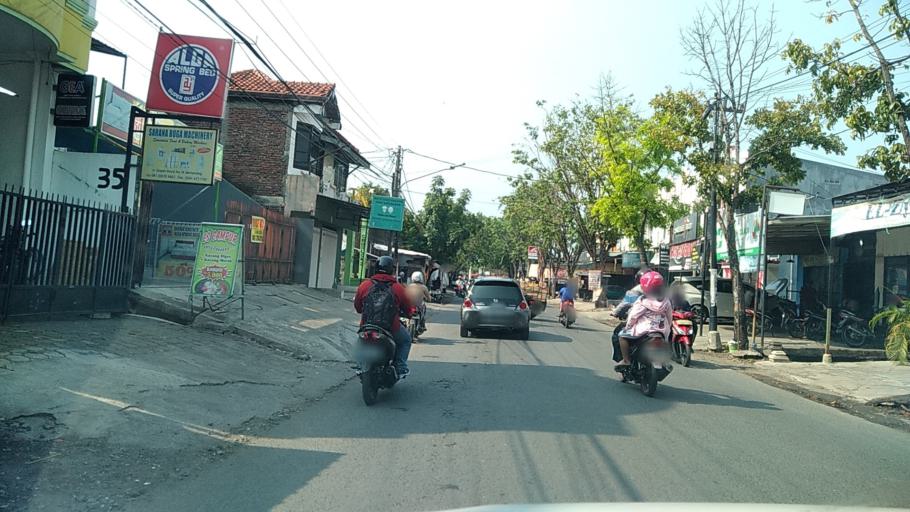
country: ID
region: Central Java
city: Semarang
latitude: -6.9792
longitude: 110.4490
